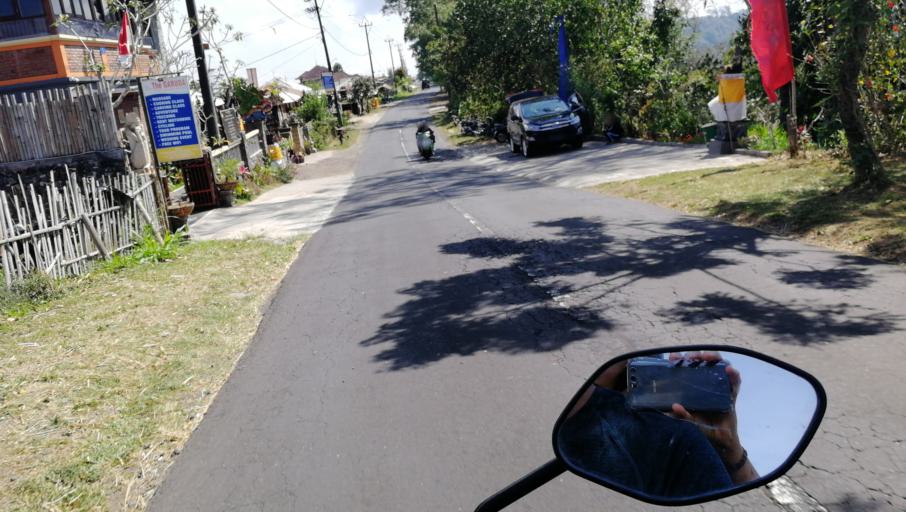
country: ID
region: Bali
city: Munduk
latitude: -8.2431
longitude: 115.1041
